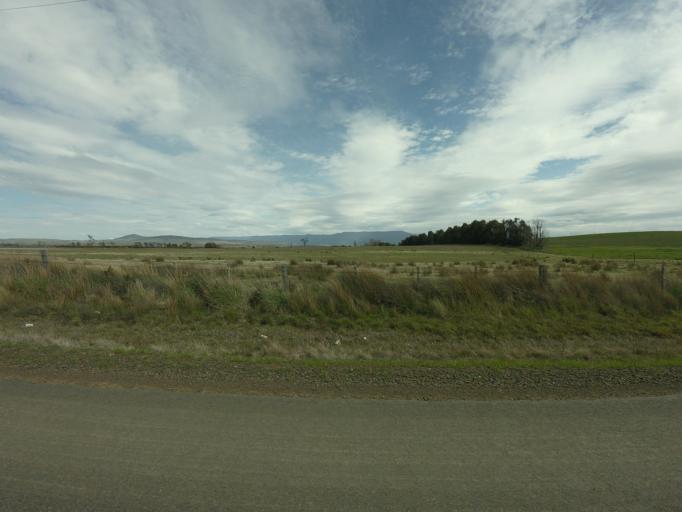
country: AU
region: Tasmania
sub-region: Northern Midlands
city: Evandale
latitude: -41.8262
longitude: 147.3203
